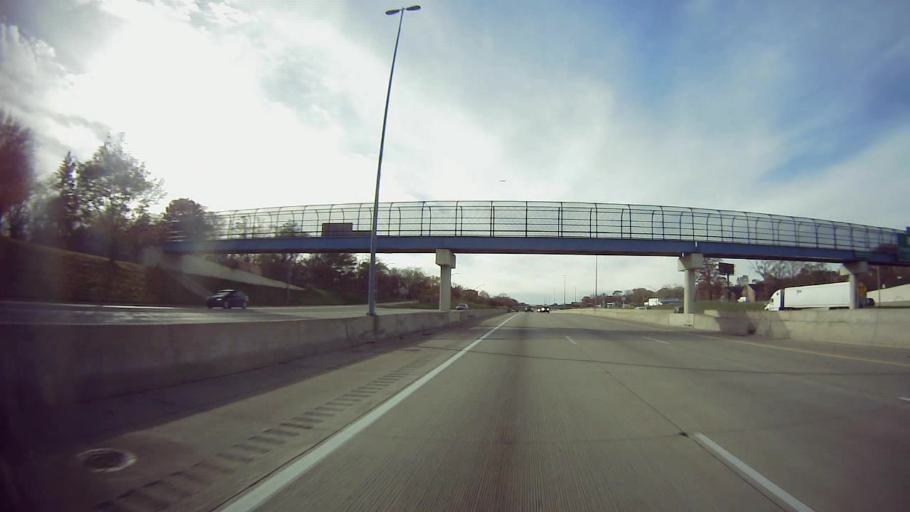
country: US
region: Michigan
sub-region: Wayne County
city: Redford
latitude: 42.3854
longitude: -83.2508
